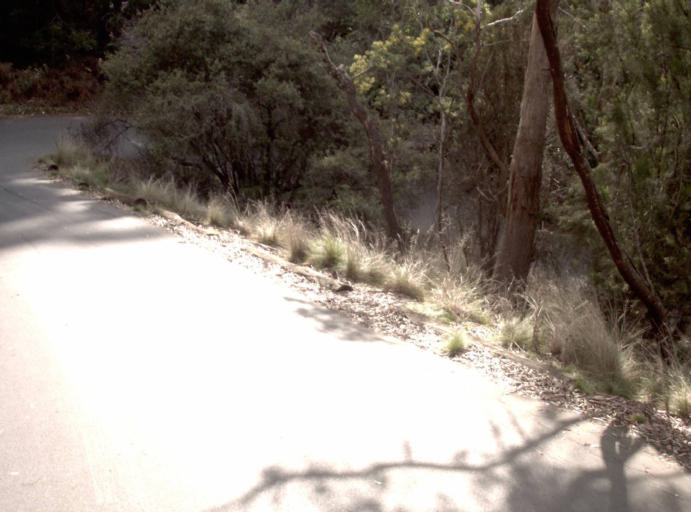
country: AU
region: Tasmania
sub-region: Launceston
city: West Launceston
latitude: -41.4430
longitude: 147.1162
